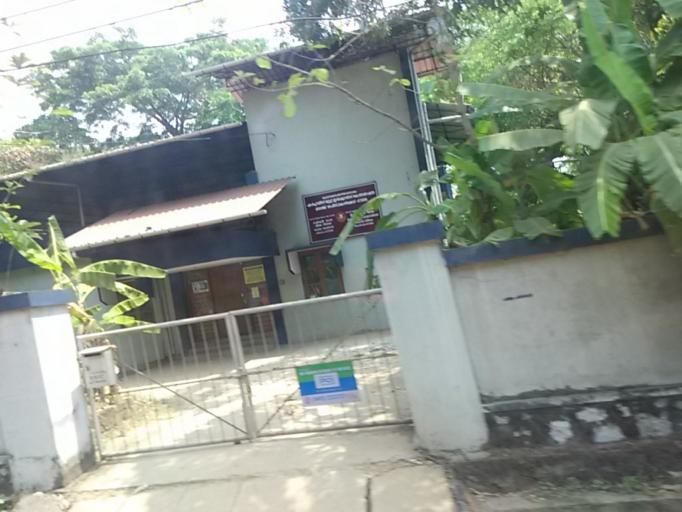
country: IN
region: Kerala
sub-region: Kozhikode
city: Kozhikode
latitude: 11.2776
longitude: 75.7715
